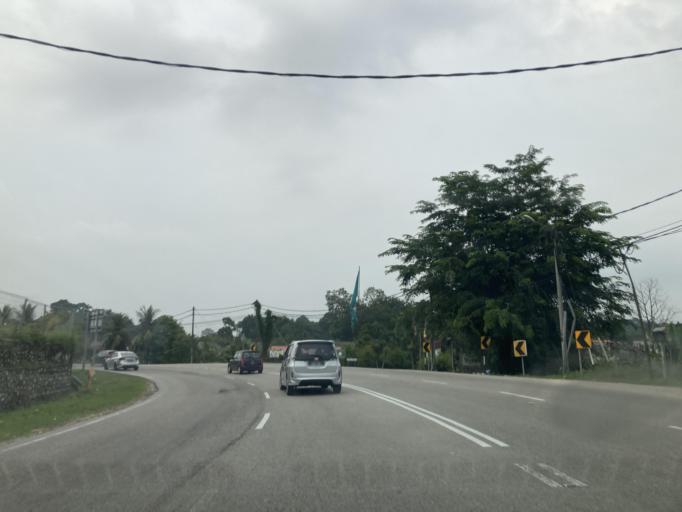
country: MY
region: Selangor
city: Kuang
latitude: 3.2138
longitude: 101.5349
